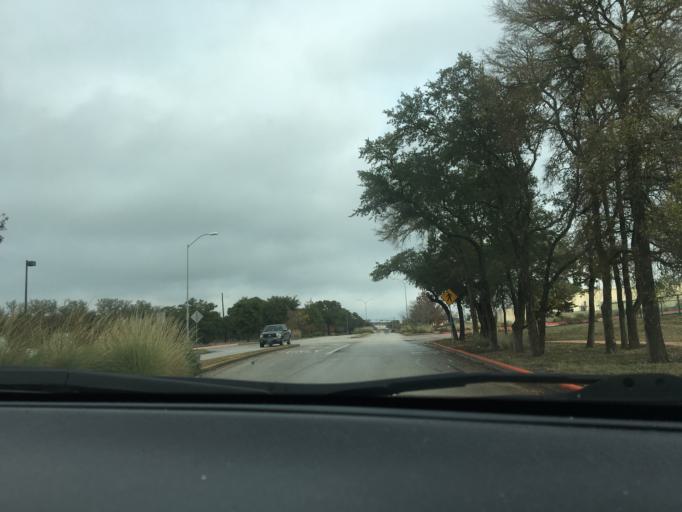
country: US
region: Texas
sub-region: Hays County
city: Dripping Springs
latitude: 30.1883
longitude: -98.0827
